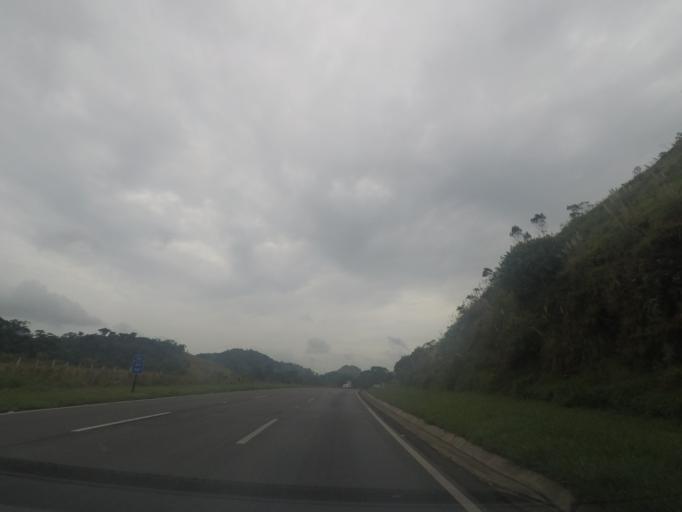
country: BR
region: Sao Paulo
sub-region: Cajati
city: Cajati
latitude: -24.8993
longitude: -48.2471
